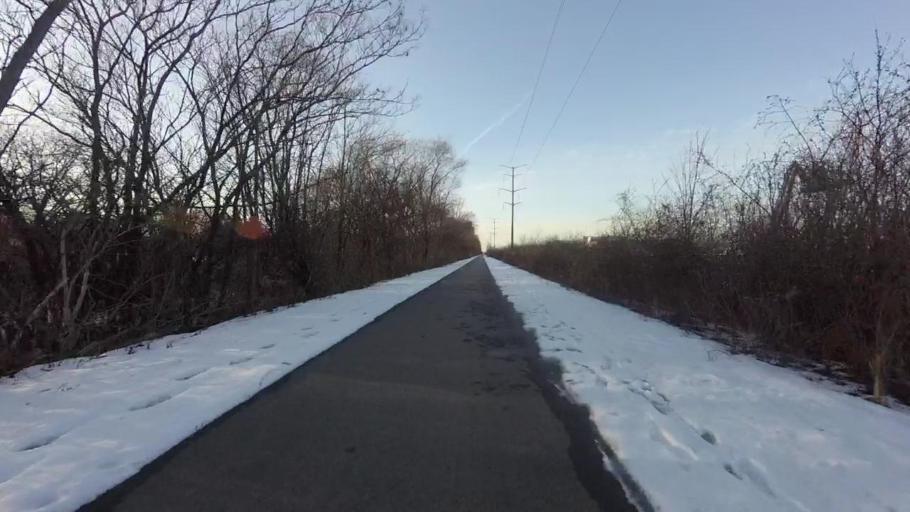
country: US
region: Wisconsin
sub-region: Milwaukee County
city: Glendale
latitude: 43.1217
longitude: -87.9356
